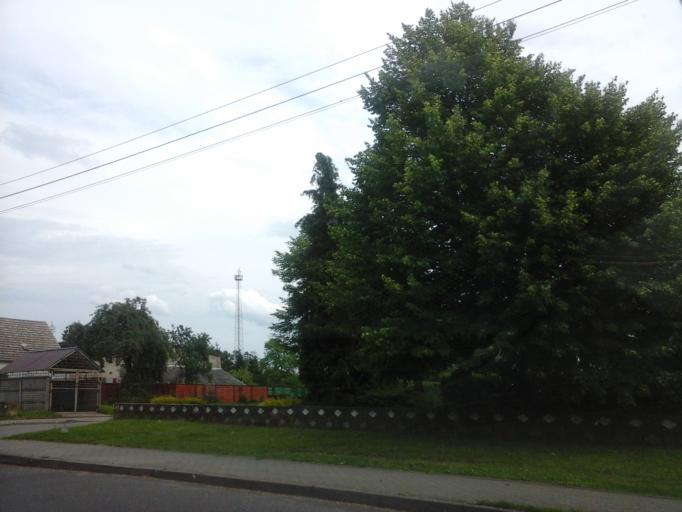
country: PL
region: West Pomeranian Voivodeship
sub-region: Powiat stargardzki
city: Suchan
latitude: 53.2797
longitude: 15.3139
